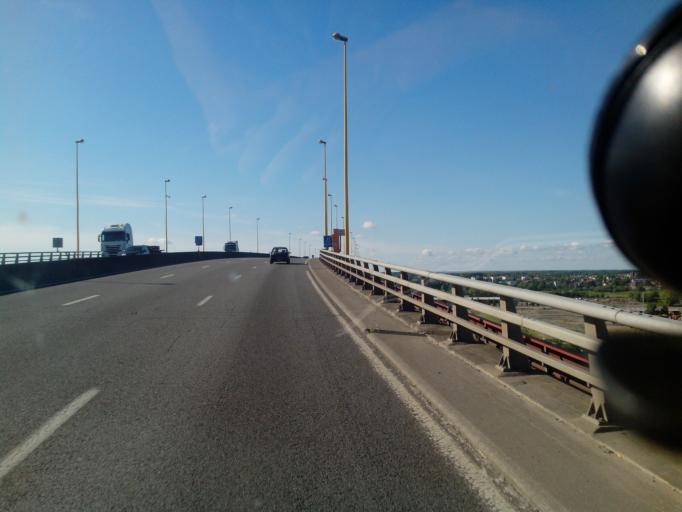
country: FR
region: Pays de la Loire
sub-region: Departement de la Loire-Atlantique
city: Bouguenais
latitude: 47.1950
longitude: -1.6138
